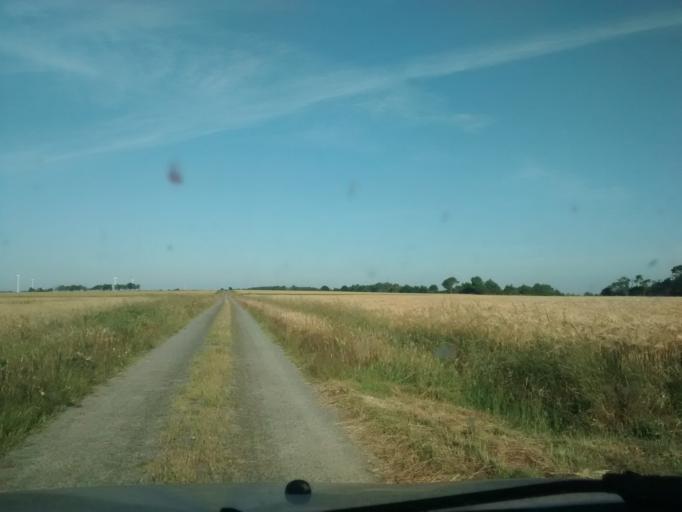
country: FR
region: Brittany
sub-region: Departement d'Ille-et-Vilaine
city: La Dominelais
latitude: 47.7880
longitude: -1.7126
